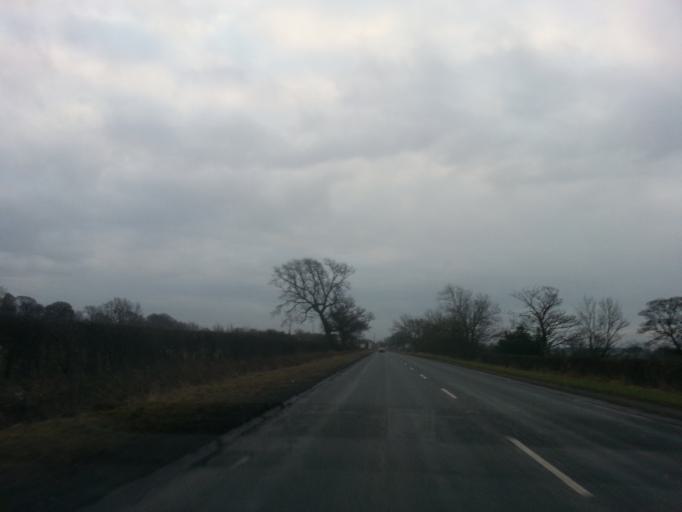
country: GB
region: England
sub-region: County Durham
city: Hamsterley
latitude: 54.7084
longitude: -1.7898
